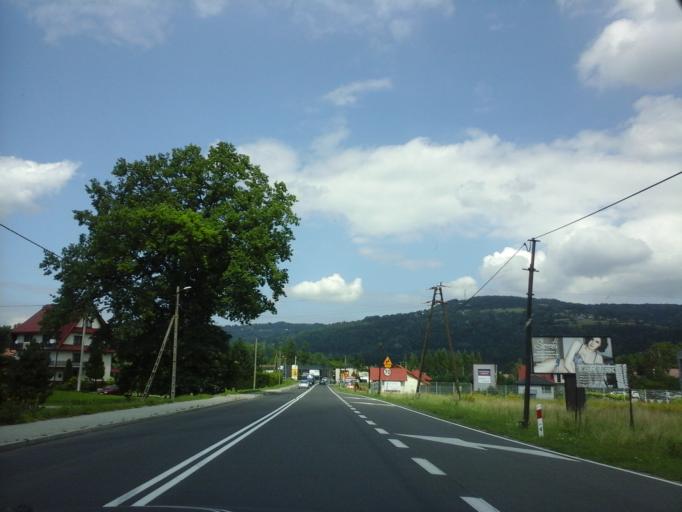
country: PL
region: Lesser Poland Voivodeship
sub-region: Powiat suski
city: Makow Podhalanski
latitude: 49.7168
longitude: 19.6879
